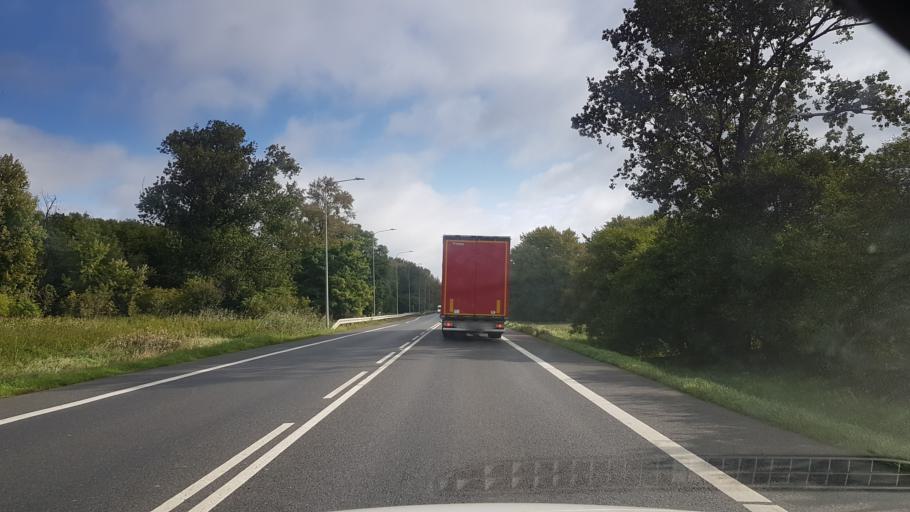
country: PL
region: Greater Poland Voivodeship
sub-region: Powiat koscianski
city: Koscian
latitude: 52.0956
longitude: 16.6332
